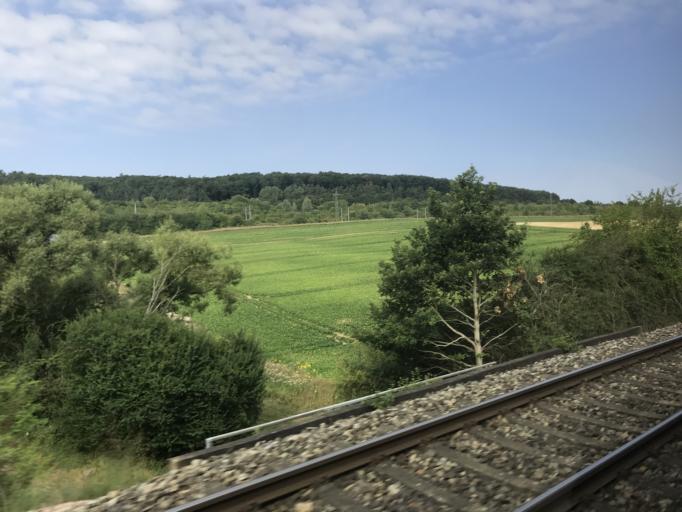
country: DE
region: Hesse
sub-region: Regierungsbezirk Darmstadt
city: Idstein
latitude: 50.2376
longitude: 8.2530
